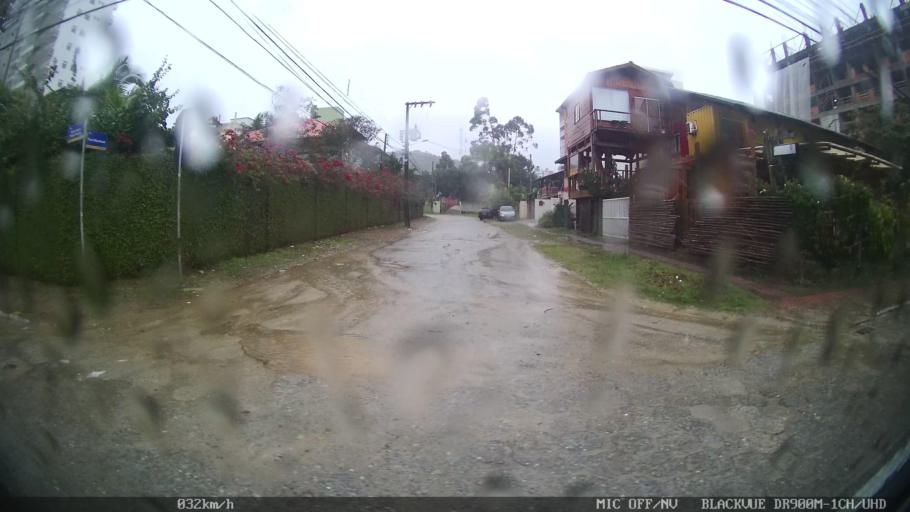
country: BR
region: Santa Catarina
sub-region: Balneario Camboriu
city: Balneario Camboriu
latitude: -26.9503
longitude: -48.6308
